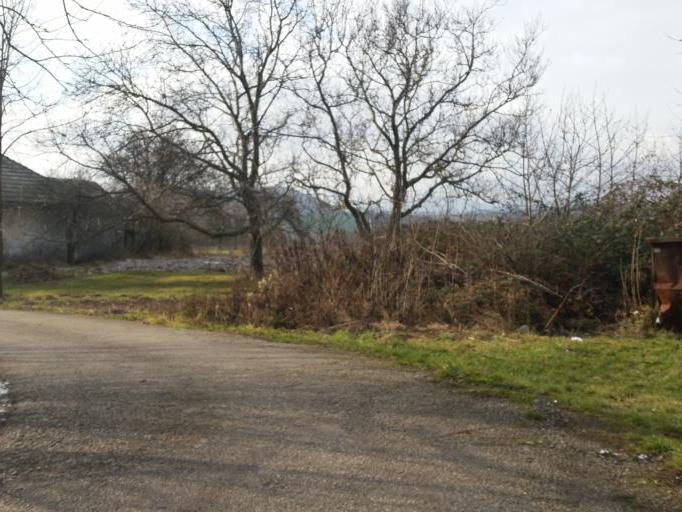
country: SK
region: Trnavsky
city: Vrbove
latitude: 48.6594
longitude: 17.7297
